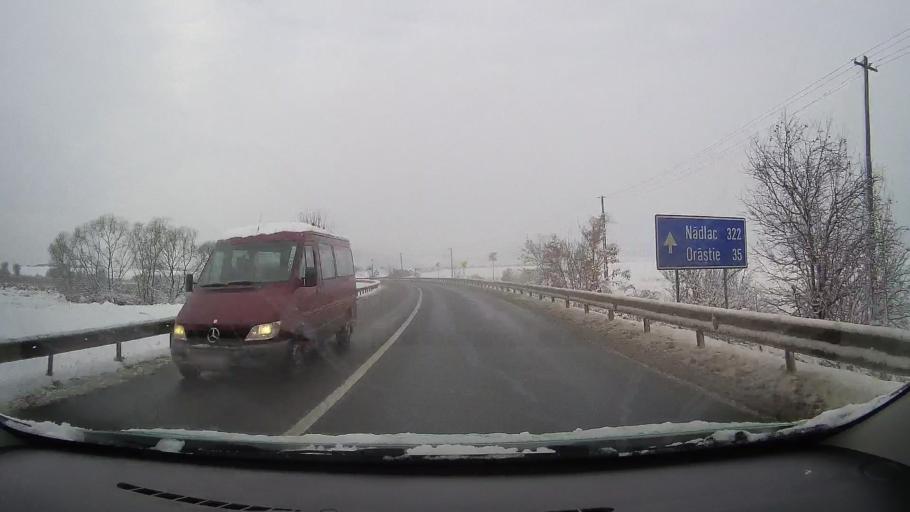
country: RO
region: Alba
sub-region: Municipiul Sebes
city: Lancram
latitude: 45.9826
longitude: 23.5169
